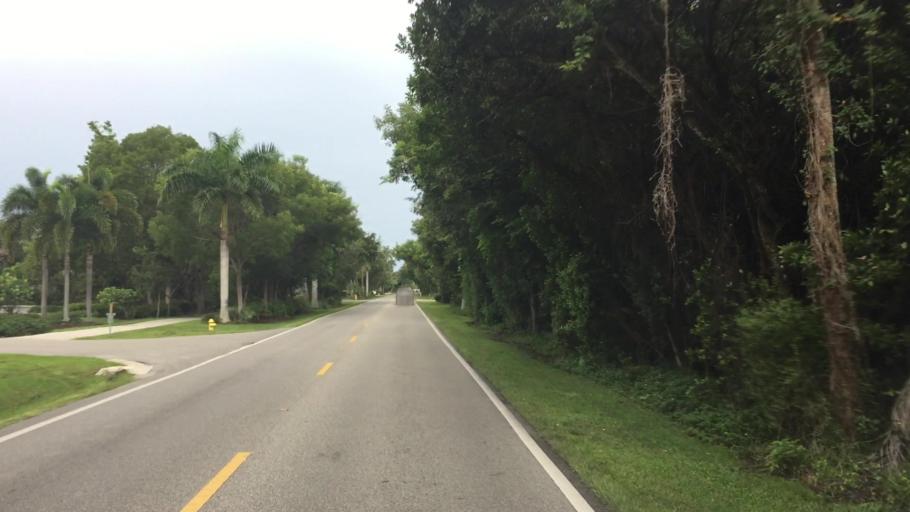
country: US
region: Florida
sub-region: Lee County
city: Sanibel
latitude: 26.4390
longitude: -82.0673
